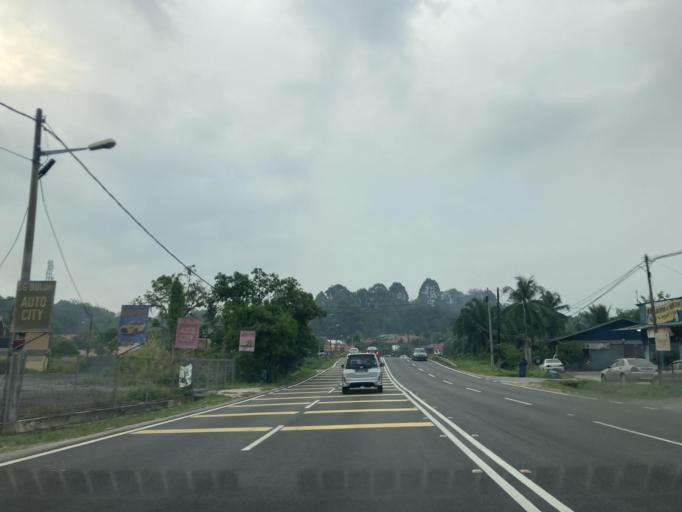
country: MY
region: Selangor
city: Kuang
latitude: 3.2100
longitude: 101.5362
